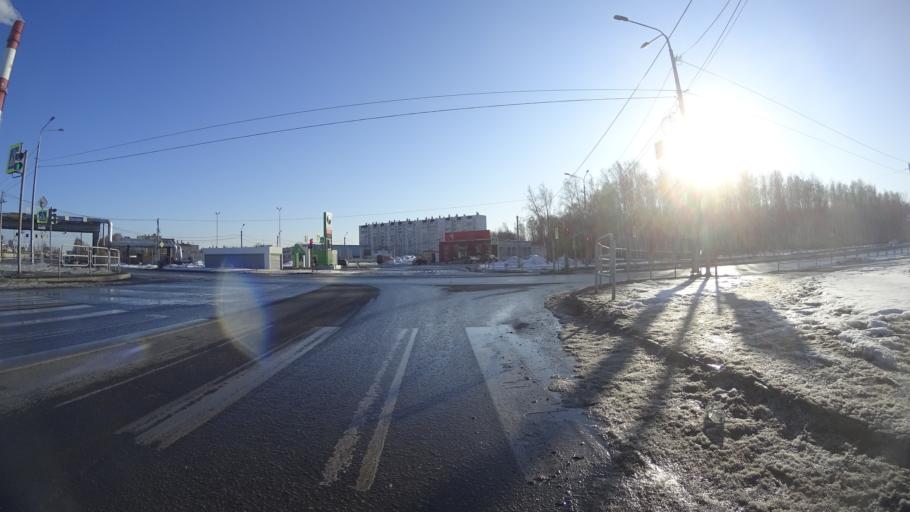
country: RU
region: Chelyabinsk
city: Roshchino
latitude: 55.2086
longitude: 61.3168
